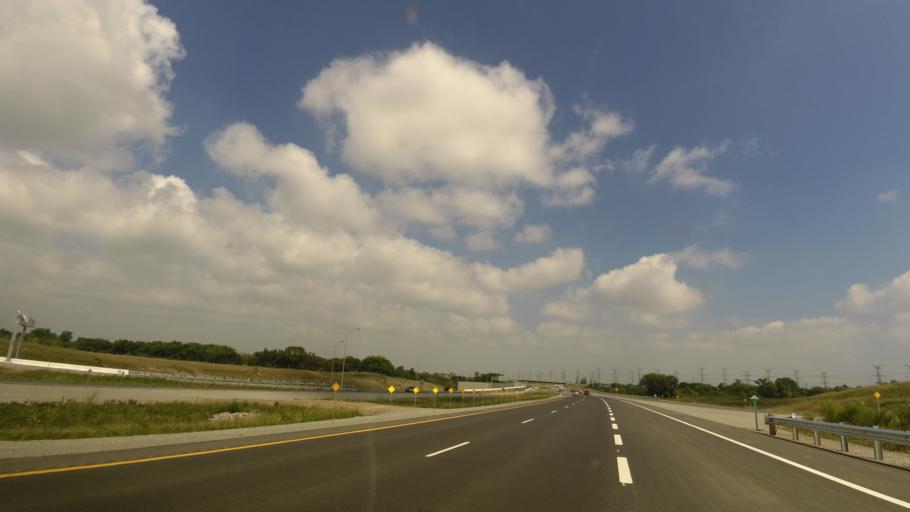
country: CA
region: Ontario
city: Oshawa
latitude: 43.9475
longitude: -78.9581
